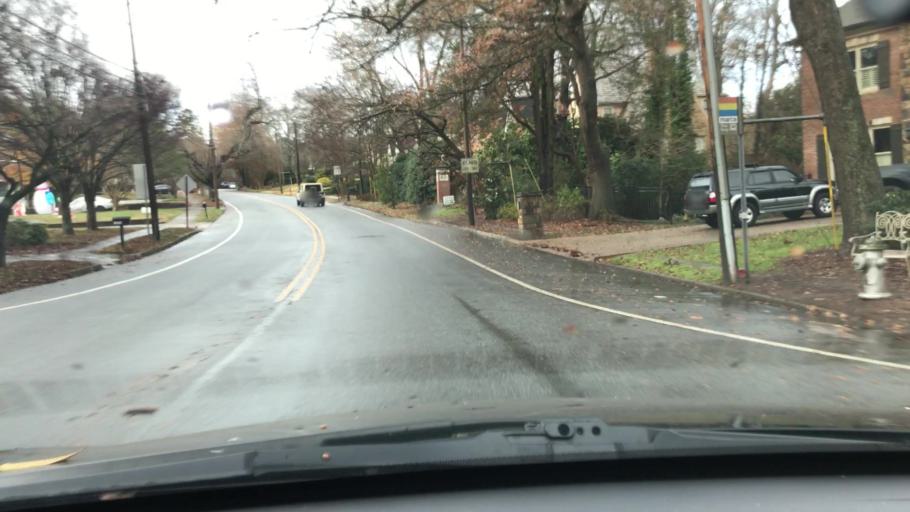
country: US
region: Georgia
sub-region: DeKalb County
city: Druid Hills
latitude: 33.7953
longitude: -84.3447
